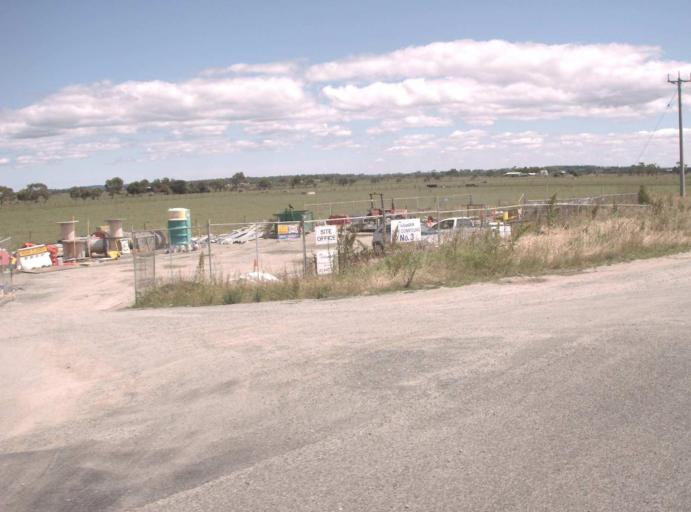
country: AU
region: Victoria
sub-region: Bass Coast
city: North Wonthaggi
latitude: -38.4844
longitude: 145.4645
